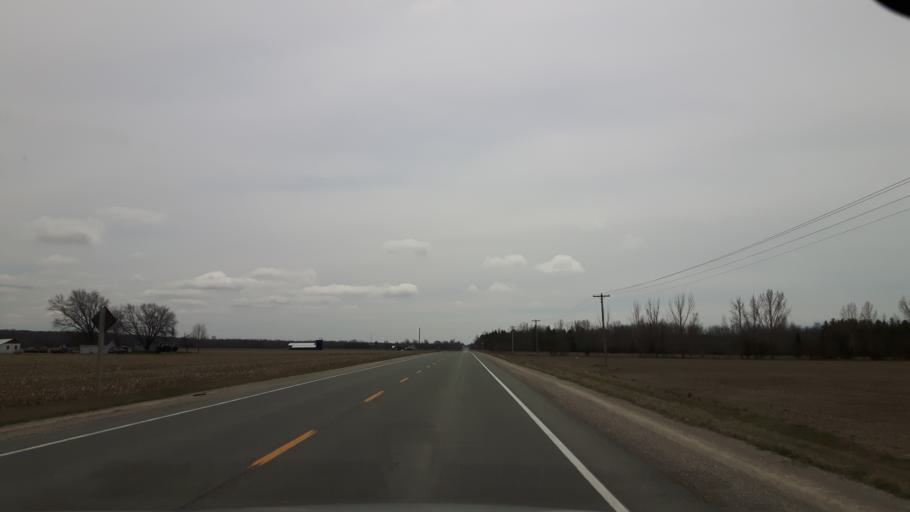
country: CA
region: Ontario
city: Goderich
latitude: 43.6284
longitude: -81.7057
